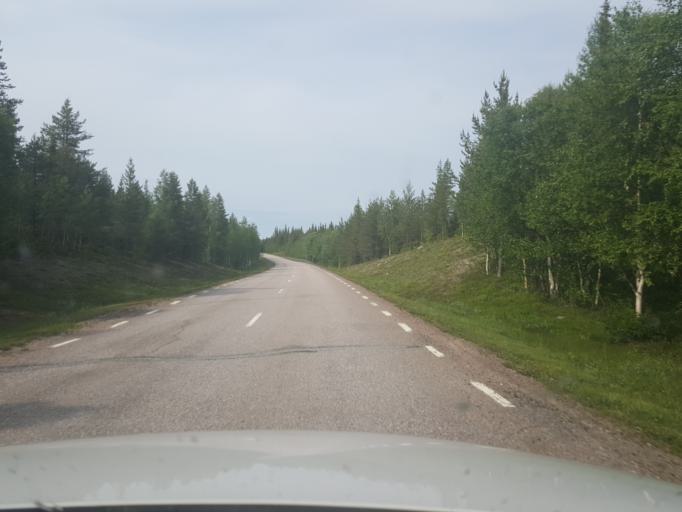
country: SE
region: Norrbotten
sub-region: Arjeplogs Kommun
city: Arjeplog
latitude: 65.8110
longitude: 18.0081
